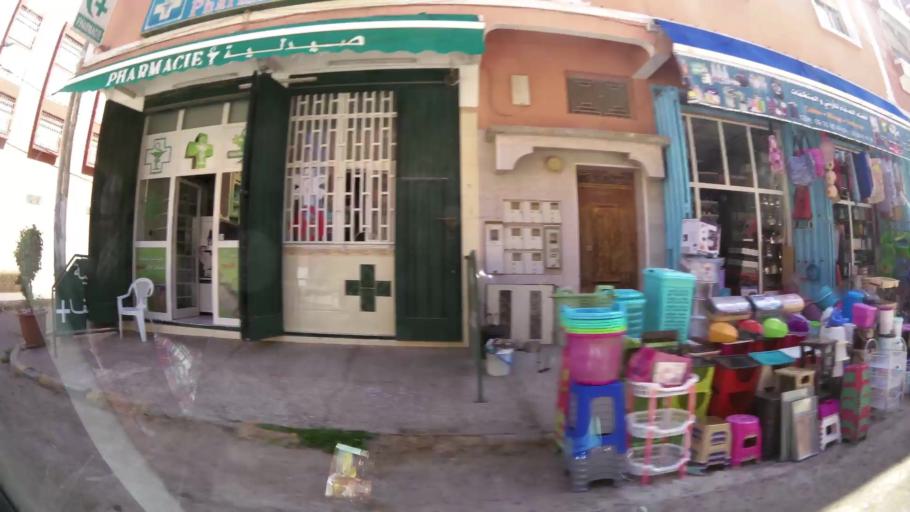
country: MA
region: Souss-Massa-Draa
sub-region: Inezgane-Ait Mellou
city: Inezgane
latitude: 30.3316
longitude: -9.5069
